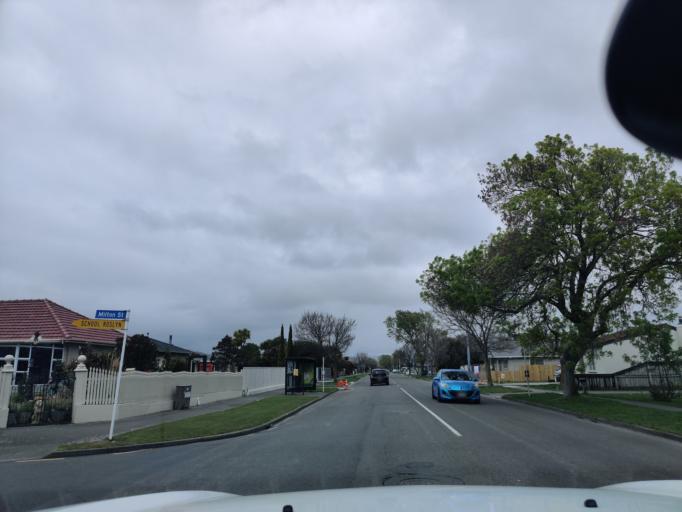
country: NZ
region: Manawatu-Wanganui
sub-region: Palmerston North City
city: Palmerston North
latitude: -40.3319
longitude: 175.6312
